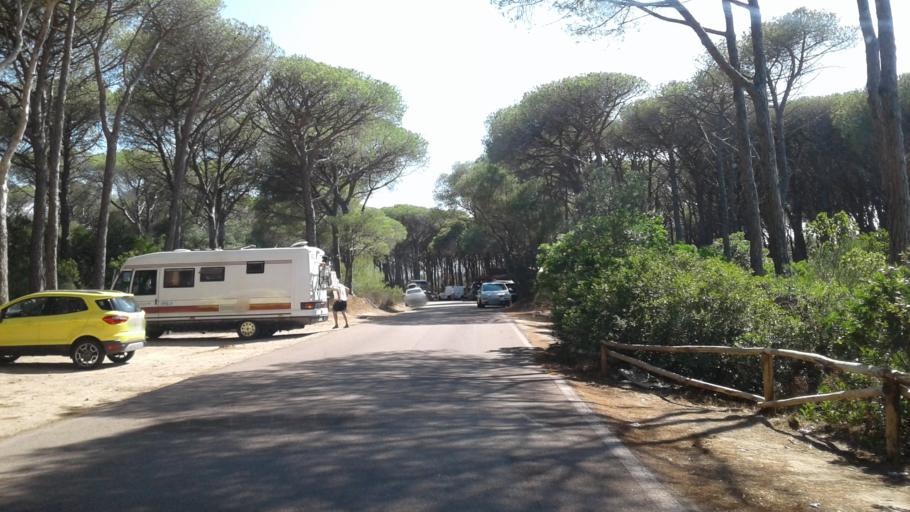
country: IT
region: Sardinia
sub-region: Provincia di Olbia-Tempio
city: La Maddalena
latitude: 41.2081
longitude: 9.4609
